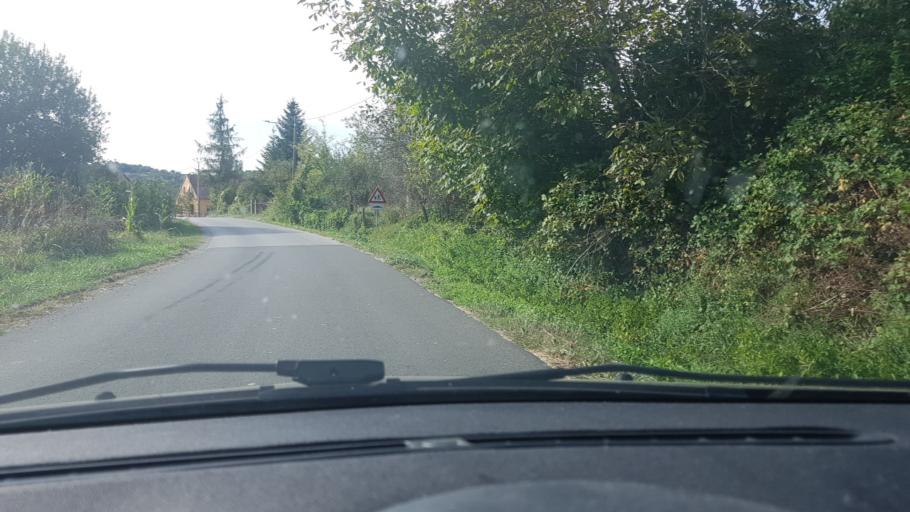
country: HR
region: Krapinsko-Zagorska
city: Zlatar
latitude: 46.1015
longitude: 16.1265
